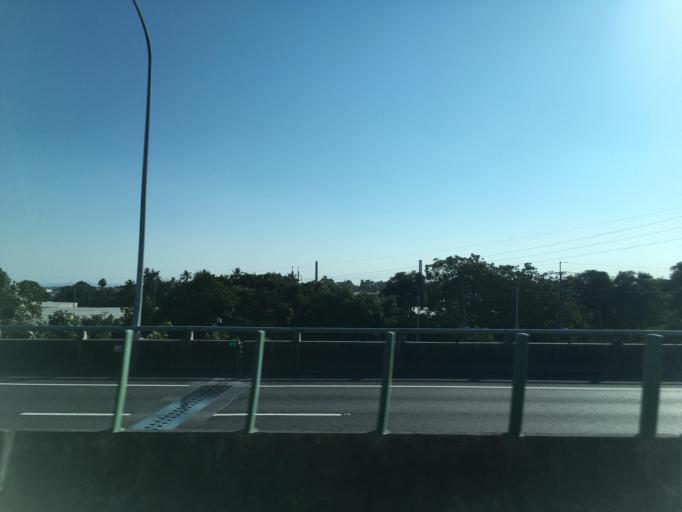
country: TW
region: Taiwan
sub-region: Chiayi
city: Taibao
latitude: 23.4191
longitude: 120.3846
